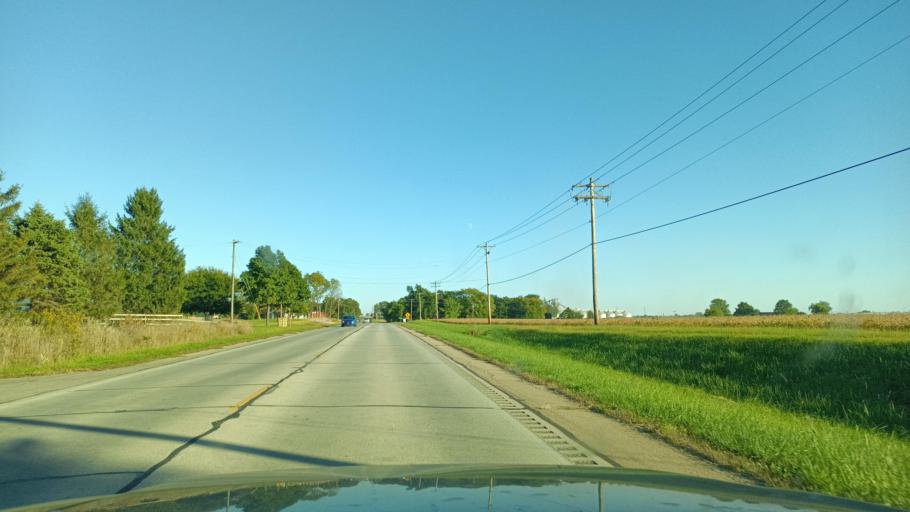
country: US
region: Illinois
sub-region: Champaign County
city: Lake of the Woods
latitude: 40.1710
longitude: -88.3371
